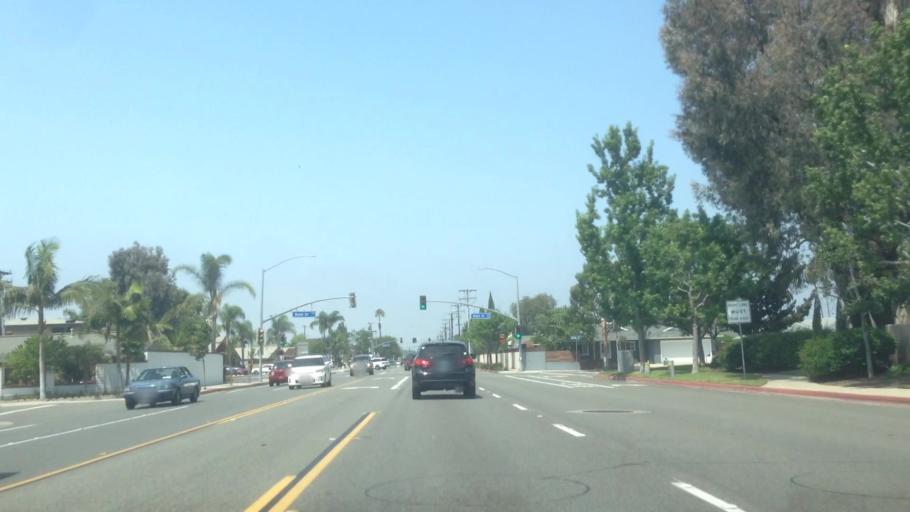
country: US
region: California
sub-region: Orange County
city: Costa Mesa
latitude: 33.6802
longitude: -117.8983
